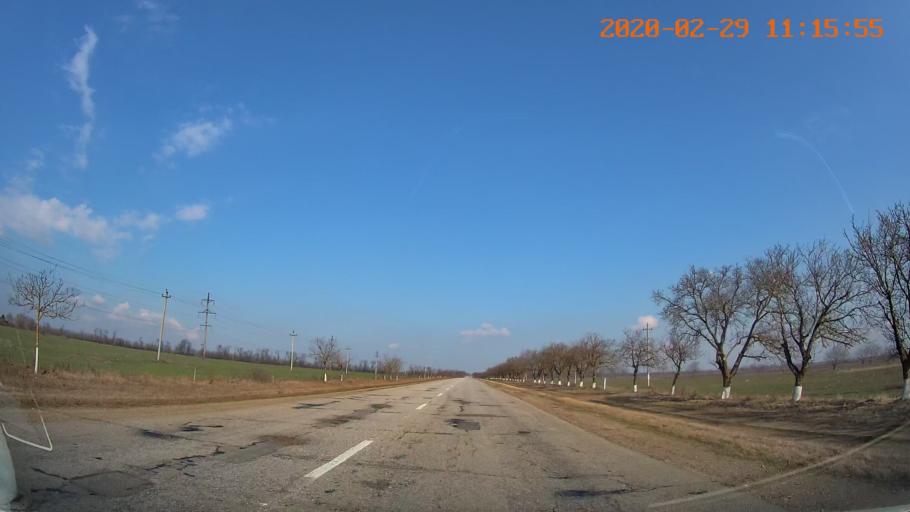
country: MD
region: Telenesti
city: Dubasari
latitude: 47.3011
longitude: 29.1663
